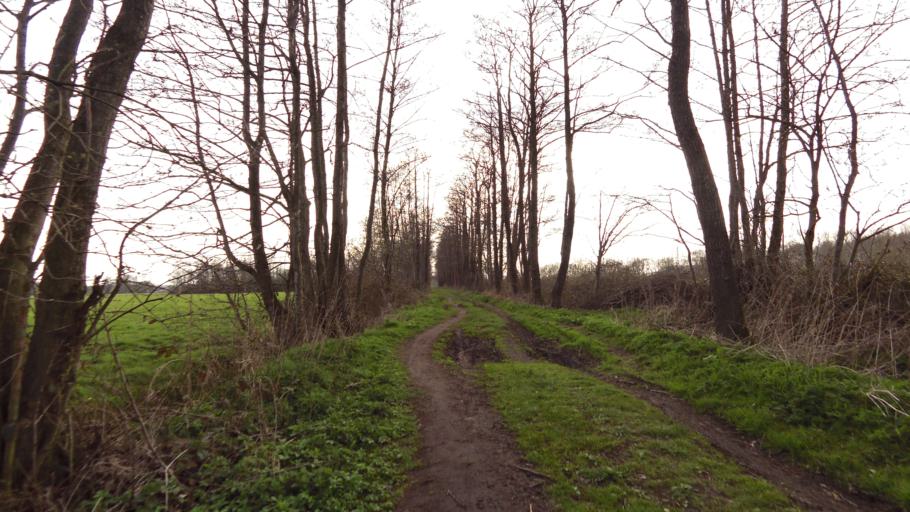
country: NL
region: Gelderland
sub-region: Gemeente Barneveld
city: Terschuur
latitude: 52.1751
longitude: 5.5228
